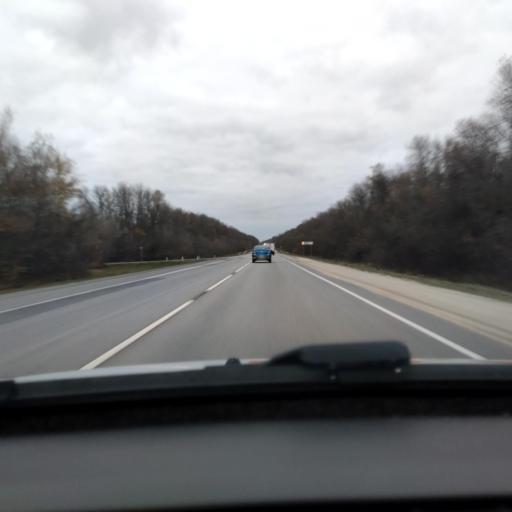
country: RU
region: Lipetsk
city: Borinskoye
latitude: 52.3827
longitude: 39.2208
